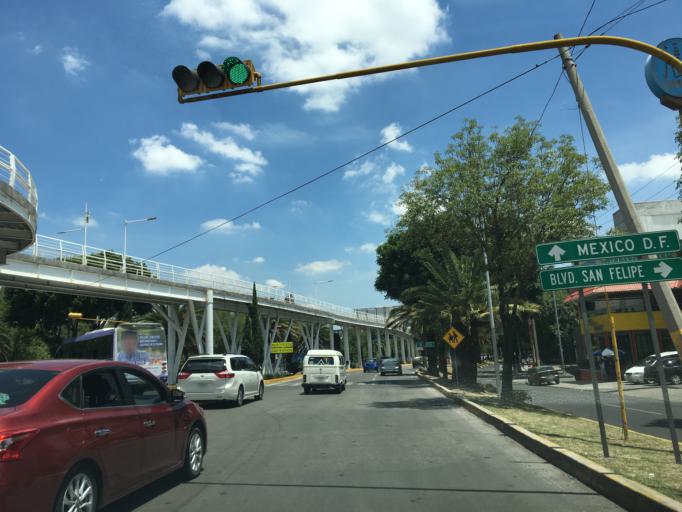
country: MX
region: Puebla
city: Puebla
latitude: 19.0637
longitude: -98.2217
